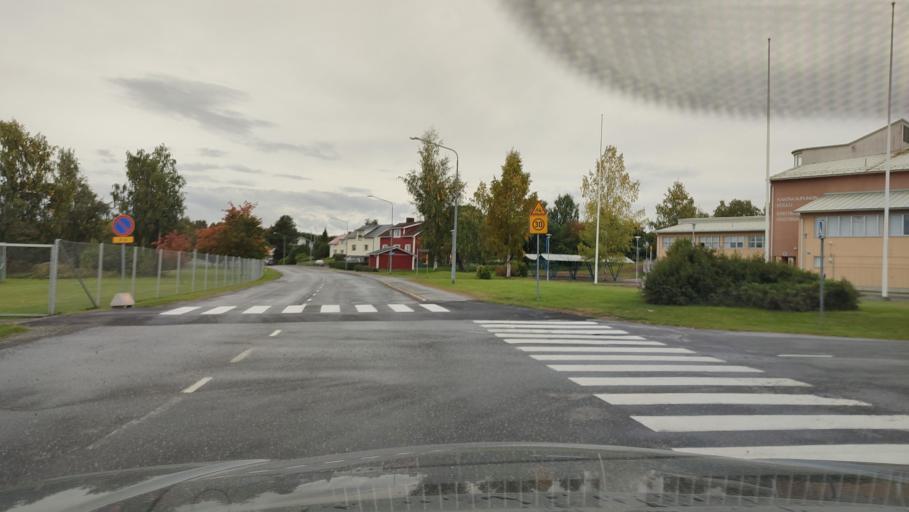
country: FI
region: Ostrobothnia
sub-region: Sydosterbotten
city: Kristinestad
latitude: 62.2794
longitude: 21.3737
